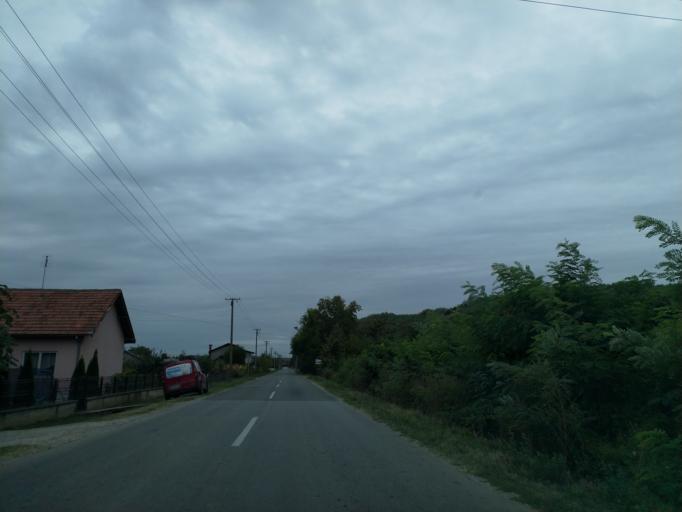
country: RS
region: Central Serbia
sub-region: Sumadijski Okrug
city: Batocina
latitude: 44.1124
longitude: 21.1499
